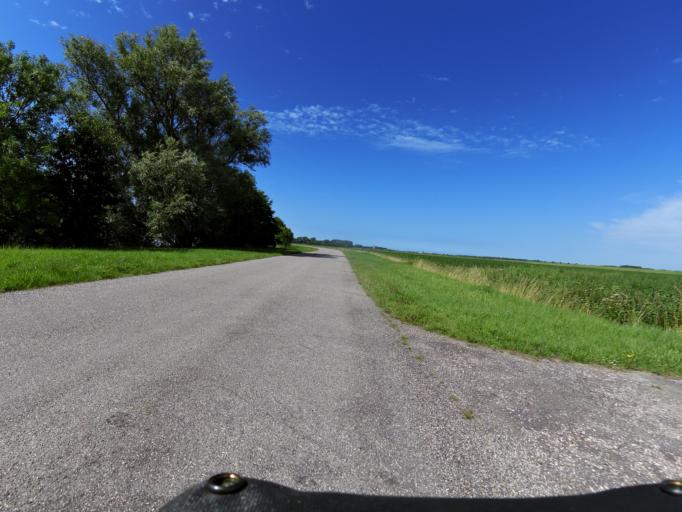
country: NL
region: Zeeland
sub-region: Gemeente Noord-Beveland
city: Kamperland
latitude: 51.5385
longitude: 3.7063
